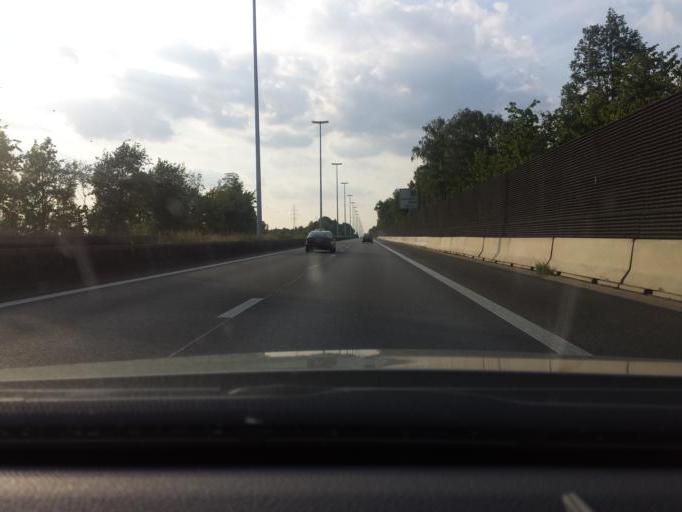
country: BE
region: Flanders
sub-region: Provincie Limburg
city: Hasselt
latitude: 50.9350
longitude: 5.2999
